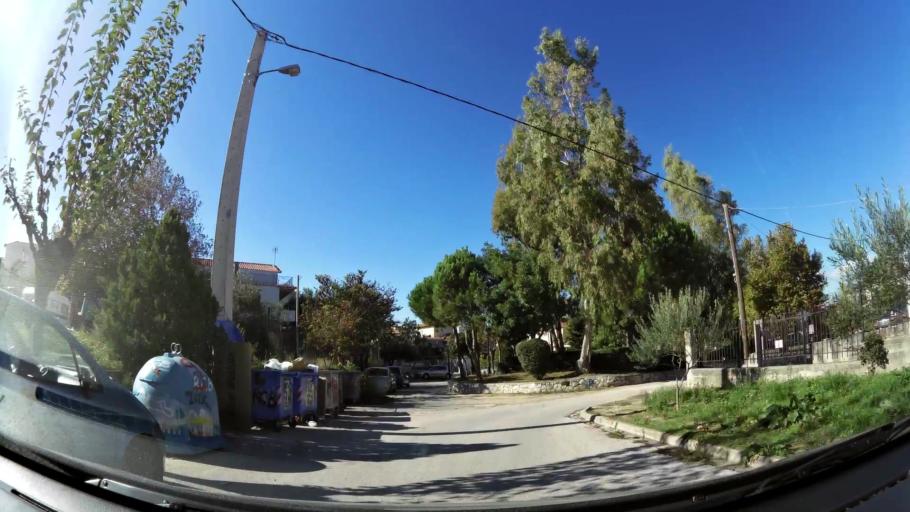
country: GR
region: Attica
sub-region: Nomarchia Anatolikis Attikis
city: Rodopoli
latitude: 38.1162
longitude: 23.8735
